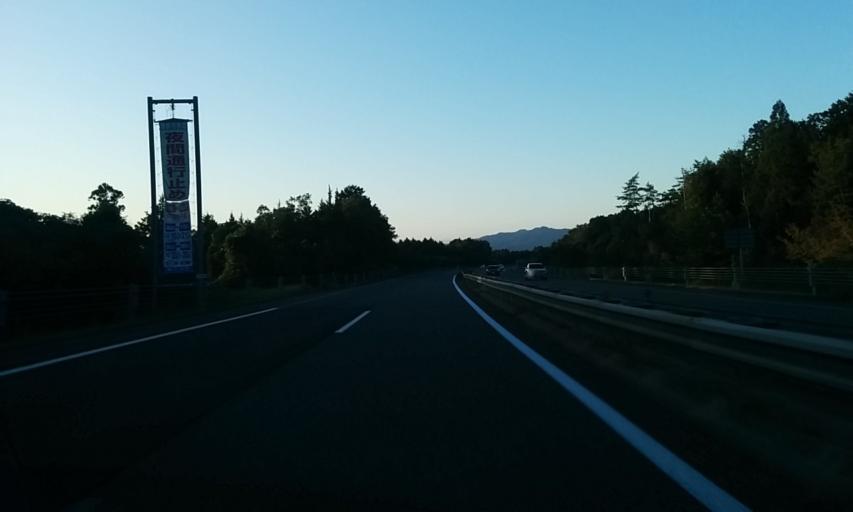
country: JP
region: Kyoto
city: Ayabe
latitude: 35.2429
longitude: 135.1836
